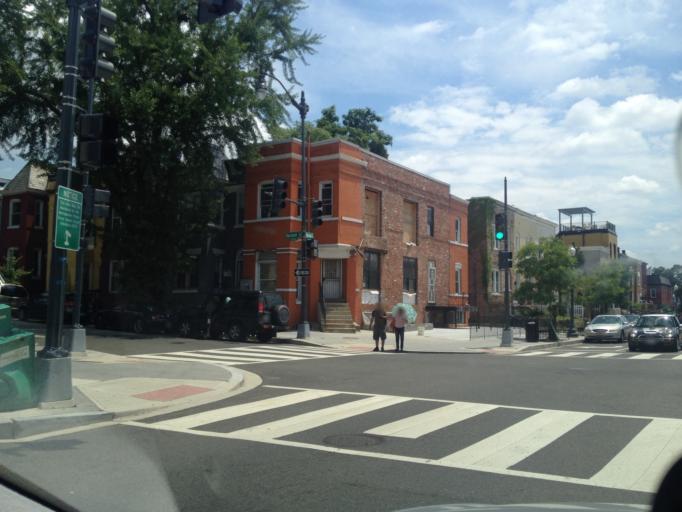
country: US
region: Washington, D.C.
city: Washington, D.C.
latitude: 38.9270
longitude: -77.0260
